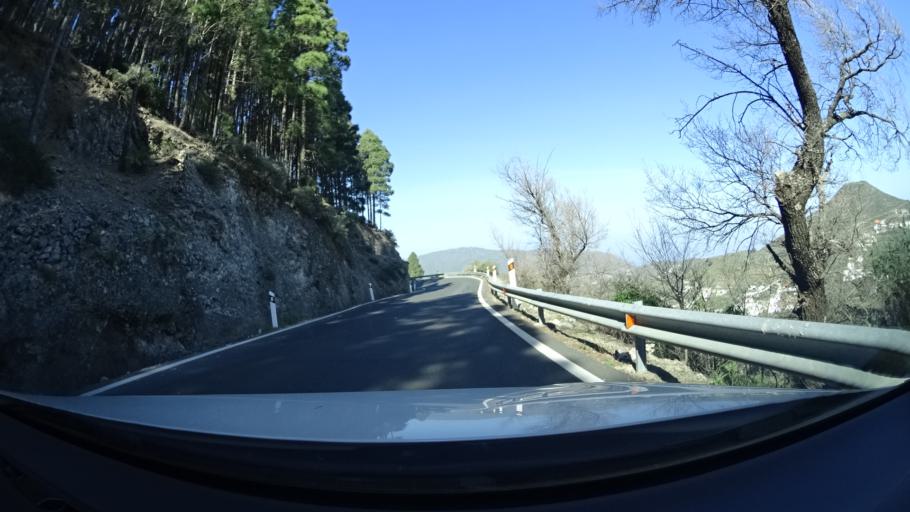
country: ES
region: Canary Islands
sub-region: Provincia de Las Palmas
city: Artenara
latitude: 28.0250
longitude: -15.6299
